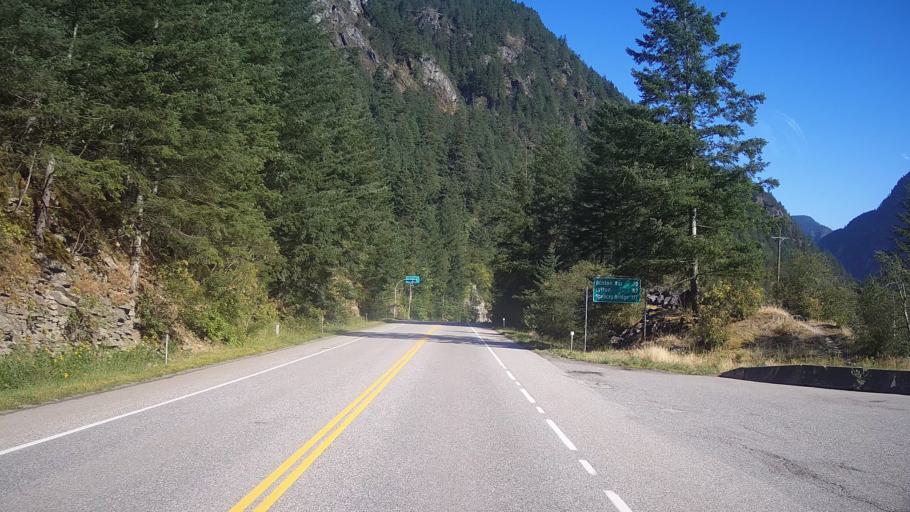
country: CA
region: British Columbia
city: Hope
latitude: 49.5676
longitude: -121.4017
